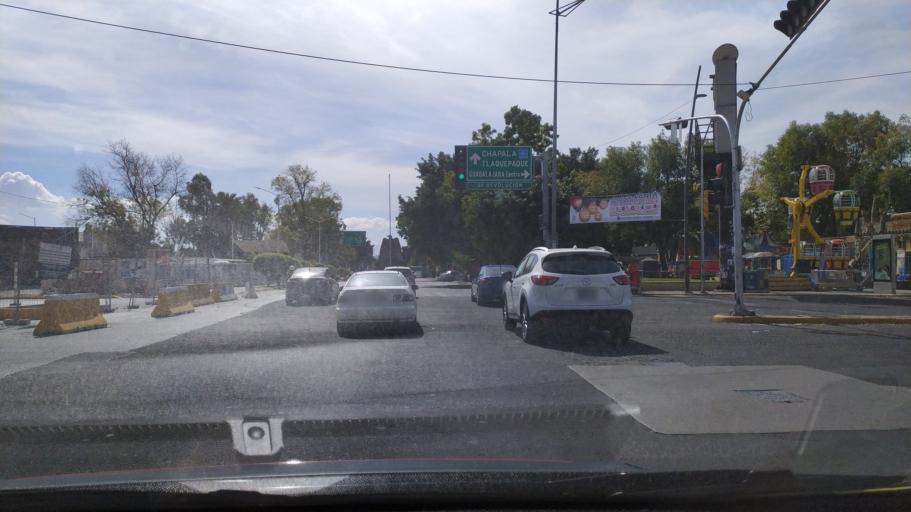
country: MX
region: Jalisco
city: Tlaquepaque
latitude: 20.6655
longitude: -103.3330
